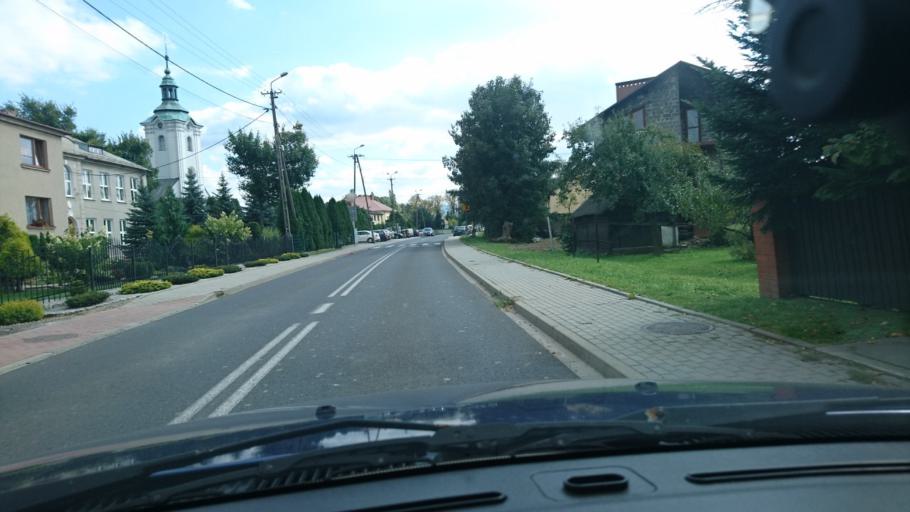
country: PL
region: Silesian Voivodeship
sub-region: Powiat bielski
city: Ligota
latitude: 49.8788
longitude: 18.9499
